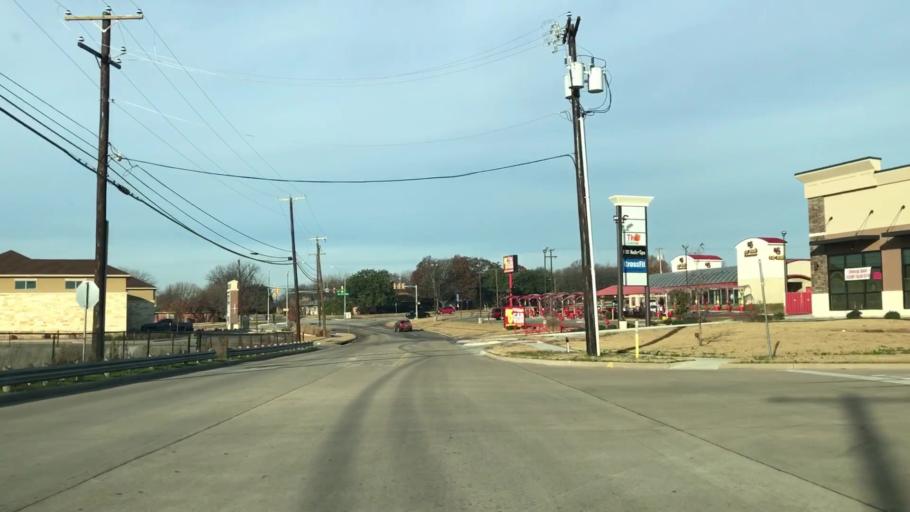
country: US
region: Texas
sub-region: Tarrant County
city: Sansom Park
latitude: 32.8173
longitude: -97.4182
